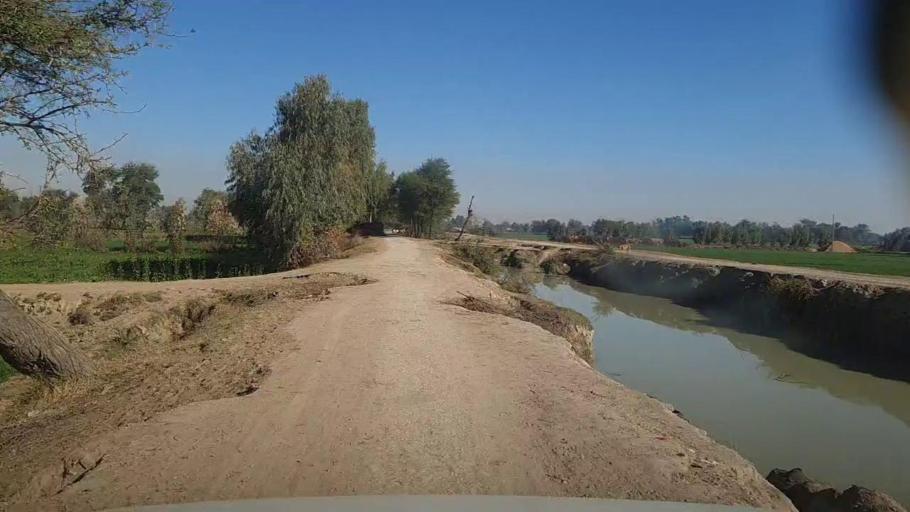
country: PK
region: Sindh
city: Khairpur
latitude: 28.0204
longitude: 69.6877
